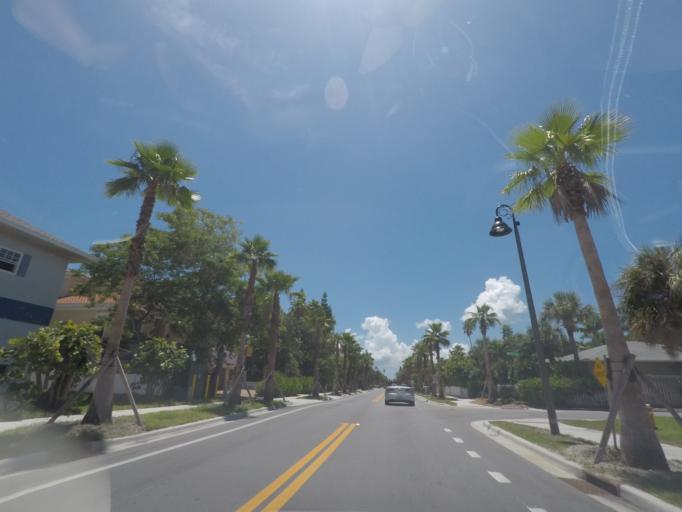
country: US
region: Florida
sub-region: Pinellas County
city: Tierra Verde
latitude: 27.7057
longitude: -82.7364
